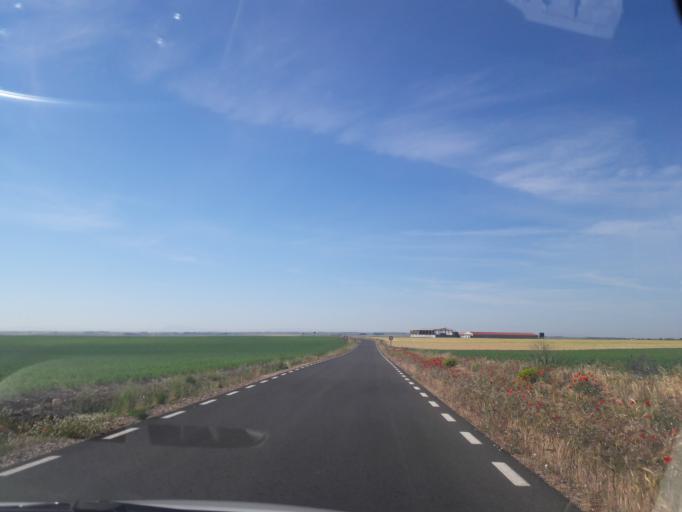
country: ES
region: Castille and Leon
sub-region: Provincia de Salamanca
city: Parada de Rubiales
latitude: 41.1321
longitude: -5.4303
